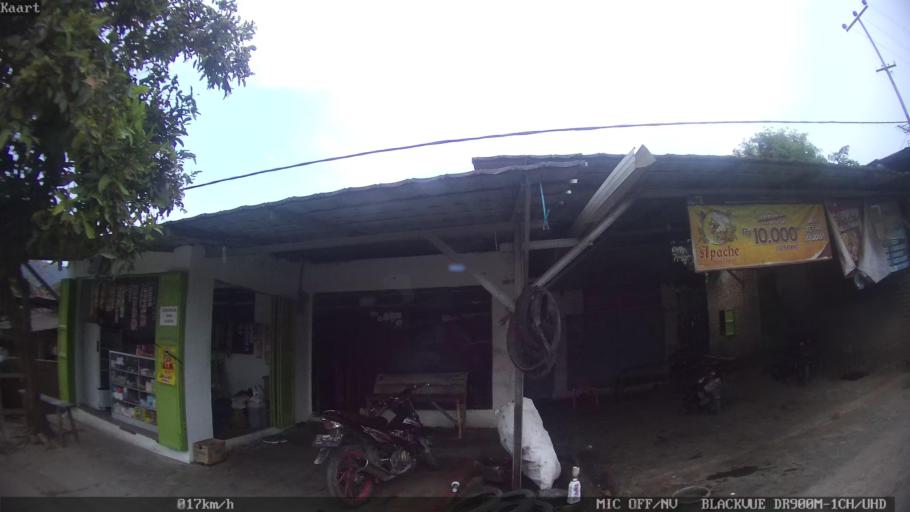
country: ID
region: Lampung
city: Panjang
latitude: -5.4355
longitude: 105.3267
